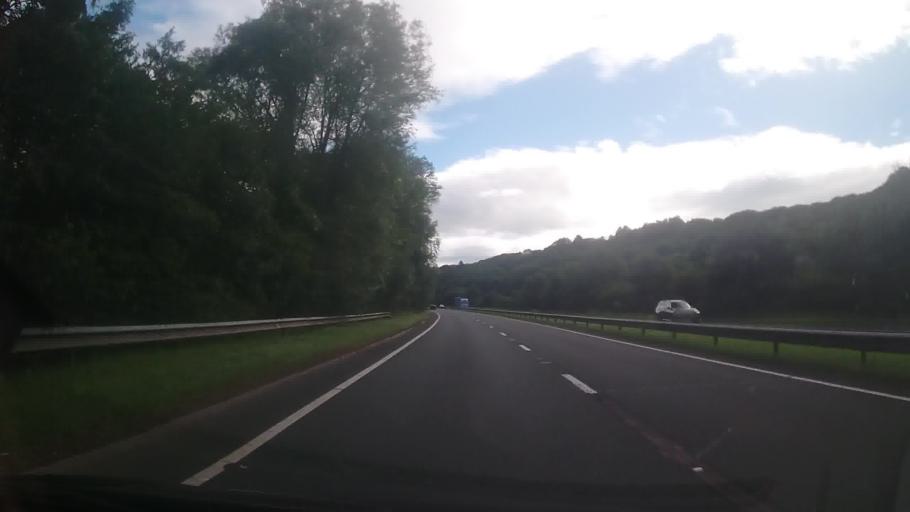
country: GB
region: Wales
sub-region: Wrexham
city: Gresford
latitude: 53.0917
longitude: -2.9769
